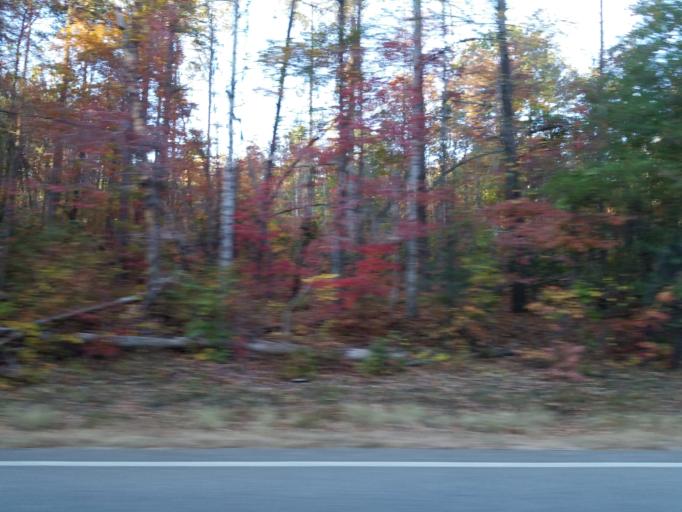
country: US
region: Georgia
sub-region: Dawson County
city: Dawsonville
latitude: 34.5509
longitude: -84.2335
